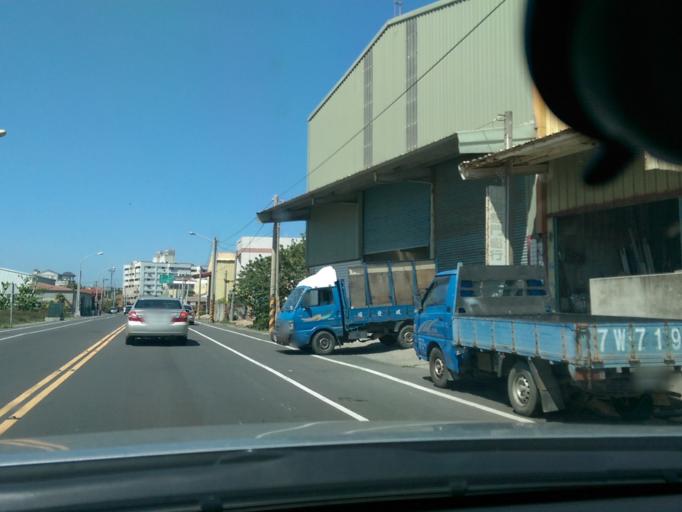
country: TW
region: Taiwan
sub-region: Yunlin
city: Douliu
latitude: 23.7412
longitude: 120.2558
